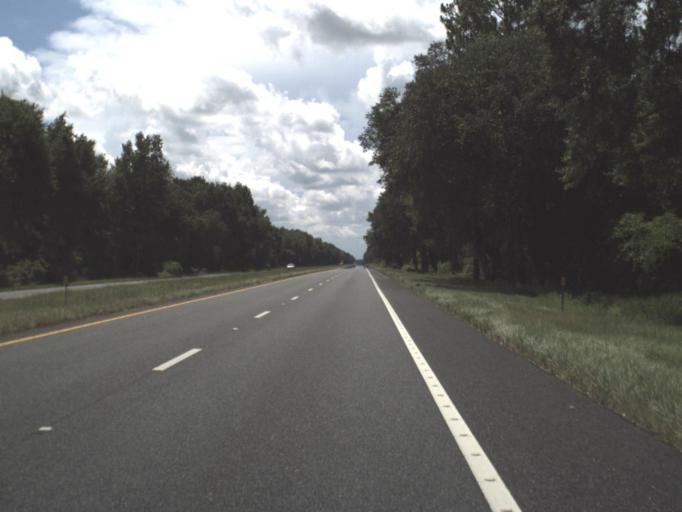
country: US
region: Florida
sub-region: Taylor County
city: Perry
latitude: 30.2220
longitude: -83.6746
